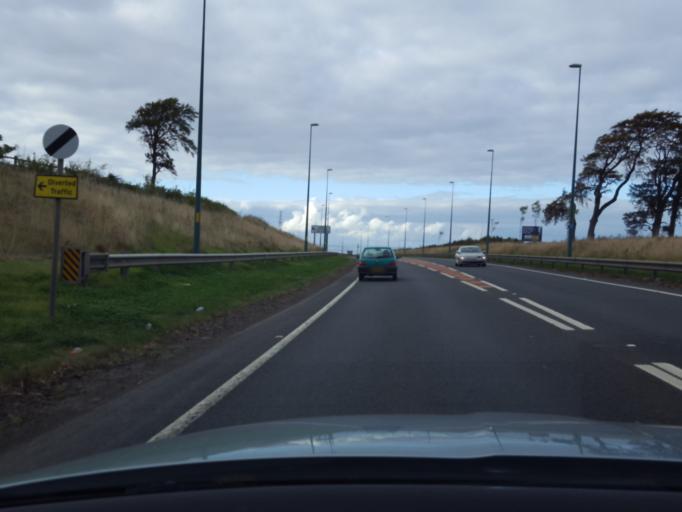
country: GB
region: Scotland
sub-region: Fife
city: Pathhead
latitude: 55.8909
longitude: -2.9970
